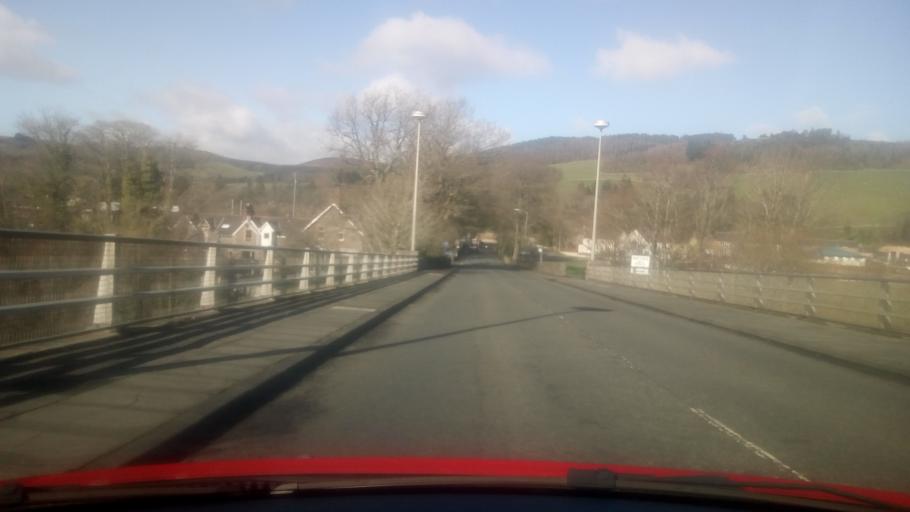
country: GB
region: Scotland
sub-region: The Scottish Borders
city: Selkirk
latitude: 55.5473
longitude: -2.8537
